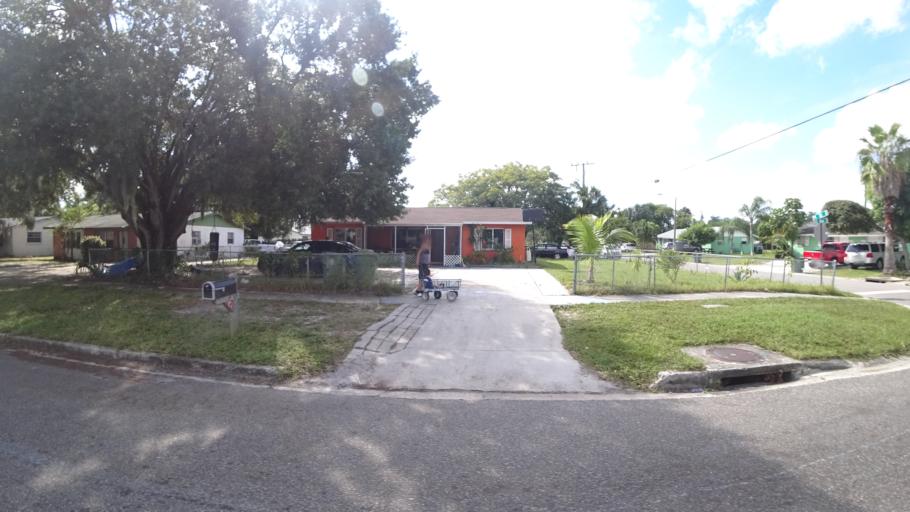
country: US
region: Florida
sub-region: Manatee County
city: Samoset
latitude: 27.4878
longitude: -82.5383
